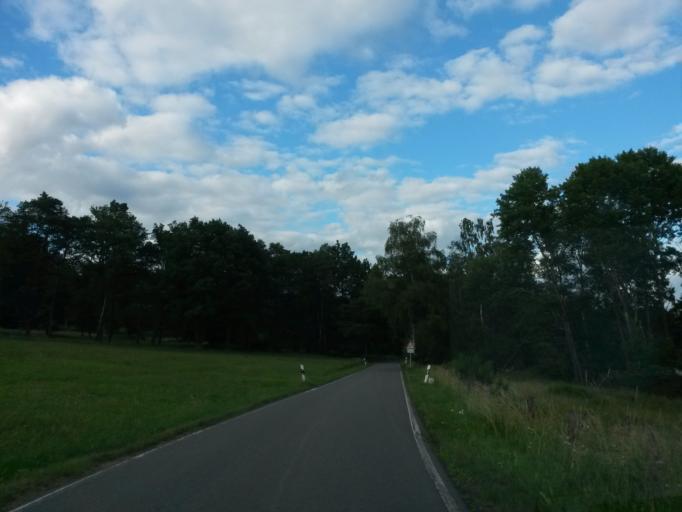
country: DE
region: North Rhine-Westphalia
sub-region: Regierungsbezirk Arnsberg
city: Drolshagen
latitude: 51.0967
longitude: 7.7373
